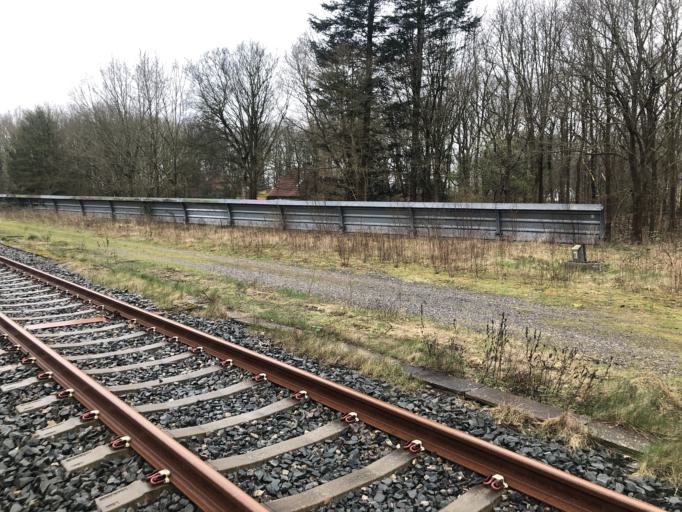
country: DK
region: South Denmark
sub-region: Aabenraa Kommune
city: Tinglev
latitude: 54.9328
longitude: 9.2568
